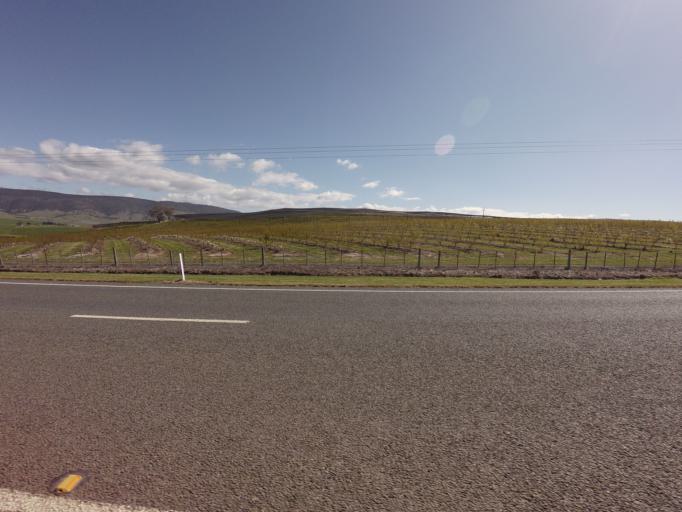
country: AU
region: Tasmania
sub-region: Derwent Valley
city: New Norfolk
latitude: -42.7108
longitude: 146.9467
